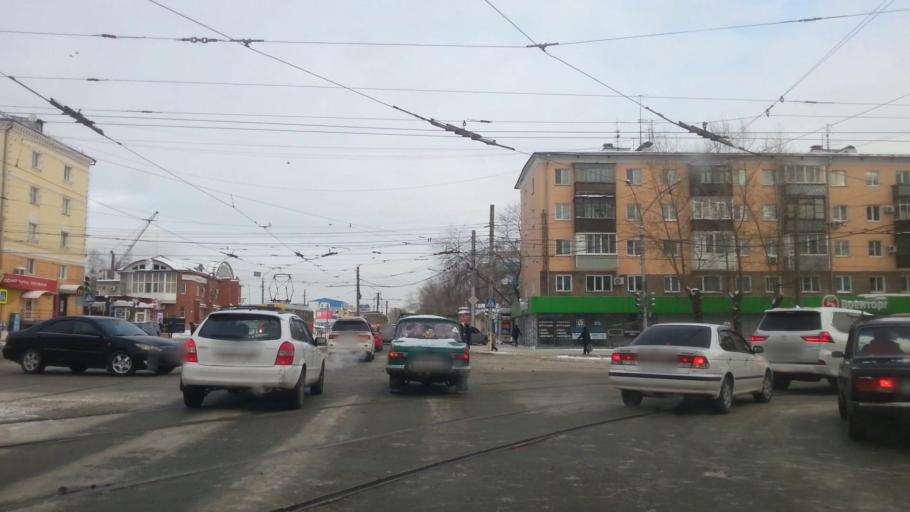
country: RU
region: Altai Krai
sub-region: Gorod Barnaulskiy
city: Barnaul
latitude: 53.3729
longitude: 83.7491
